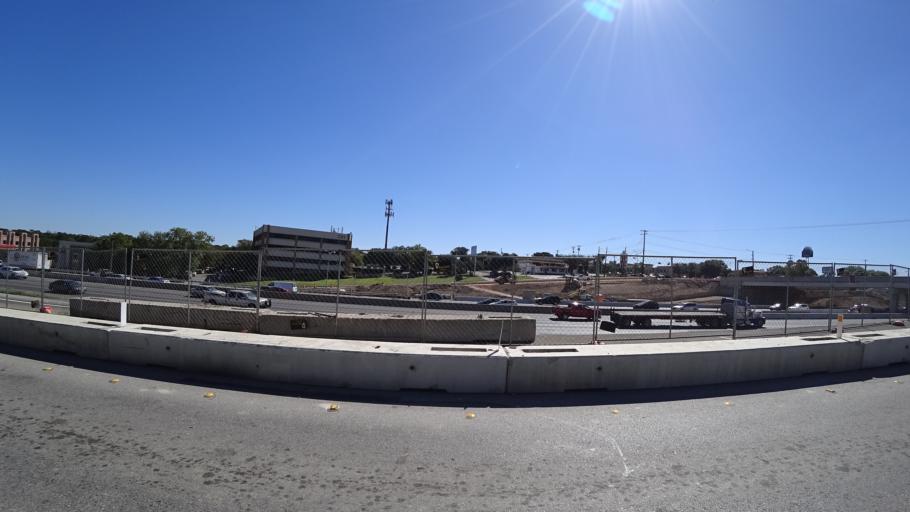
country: US
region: Texas
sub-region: Travis County
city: Austin
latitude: 30.2349
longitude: -97.7411
